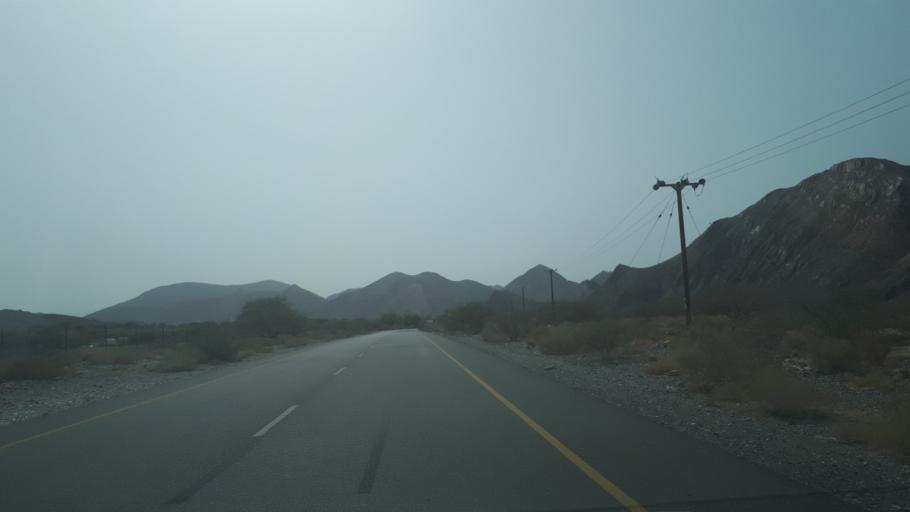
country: OM
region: Muhafazat ad Dakhiliyah
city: Bahla'
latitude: 23.2209
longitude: 56.9996
